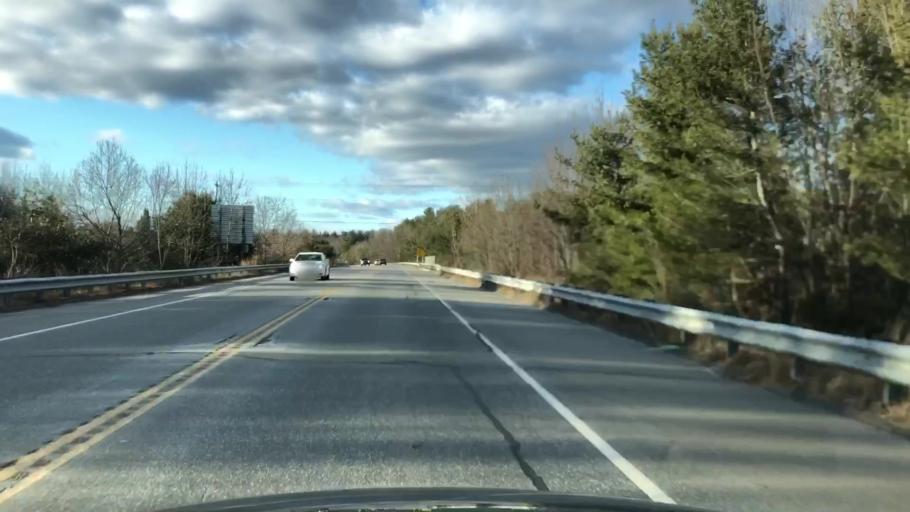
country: US
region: New Hampshire
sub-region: Hillsborough County
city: Milford
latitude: 42.8229
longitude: -71.6598
